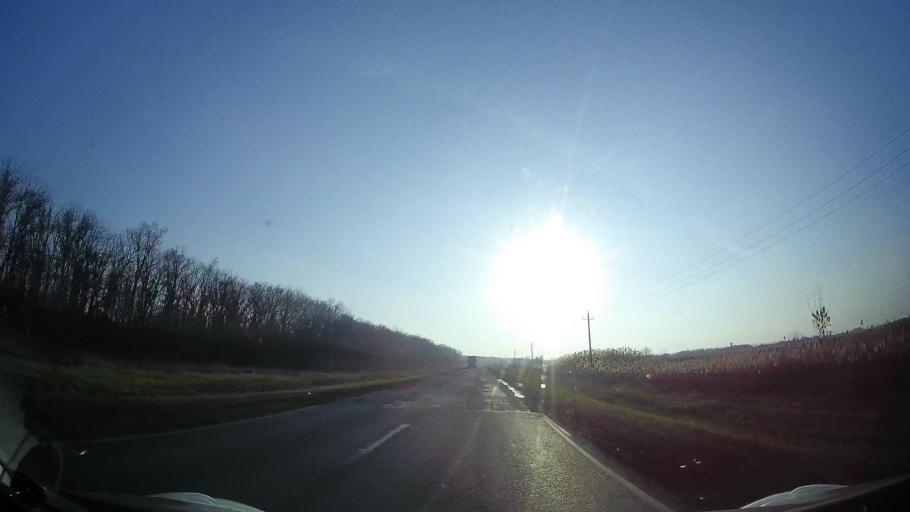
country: RU
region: Rostov
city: Ol'ginskaya
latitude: 47.1430
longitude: 39.9022
